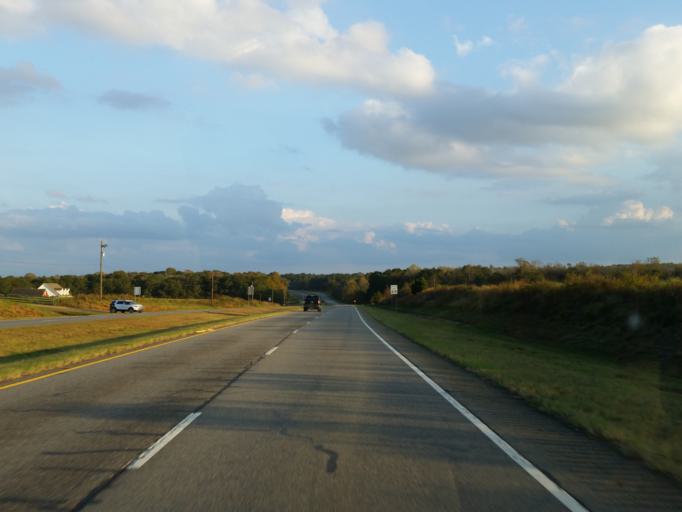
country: US
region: Georgia
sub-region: Houston County
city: Perry
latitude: 32.4313
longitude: -83.7193
